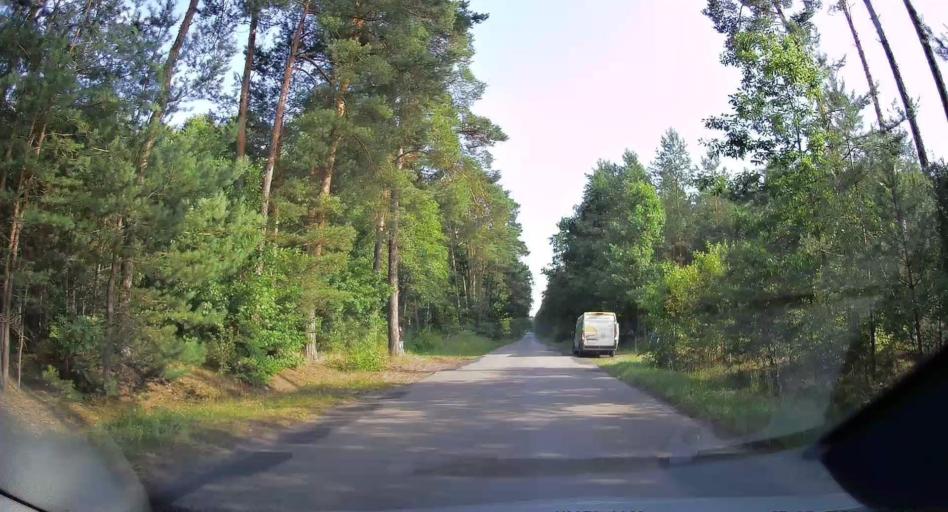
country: PL
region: Swietokrzyskie
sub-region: Powiat konecki
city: Konskie
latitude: 51.2329
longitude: 20.3823
